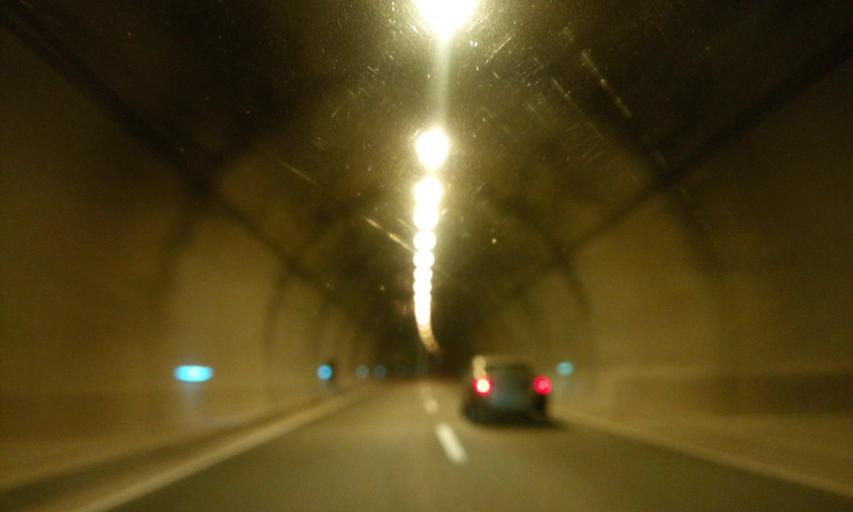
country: TR
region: Bilecik
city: Vezirhan
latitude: 40.1903
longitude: 30.0143
